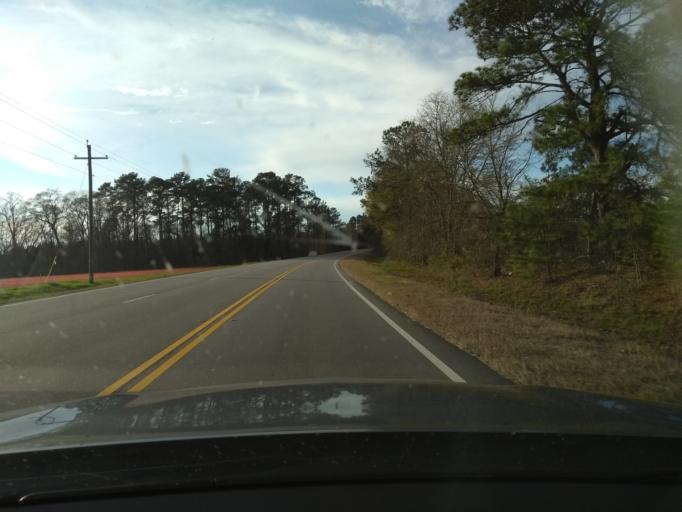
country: US
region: Georgia
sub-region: Bulloch County
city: Brooklet
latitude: 32.2944
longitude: -81.7692
